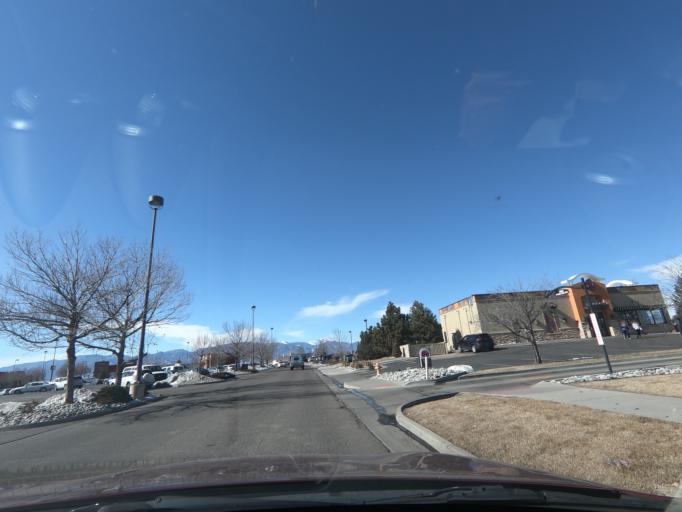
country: US
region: Colorado
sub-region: El Paso County
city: Security-Widefield
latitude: 38.7177
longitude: -104.6989
